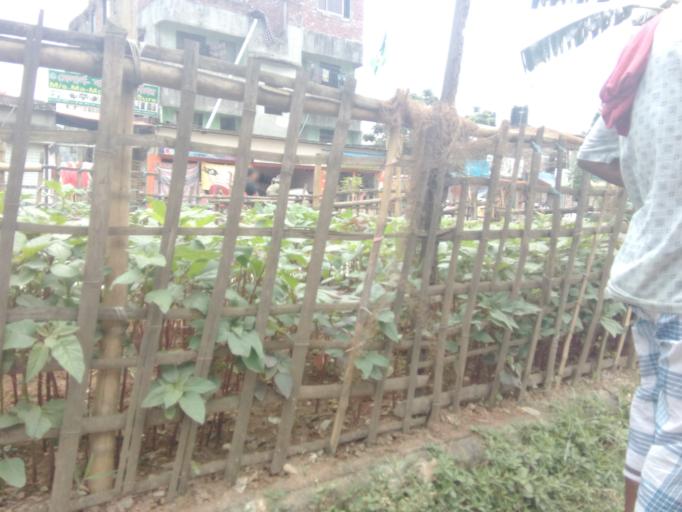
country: BD
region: Dhaka
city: Paltan
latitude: 23.7987
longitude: 90.4323
